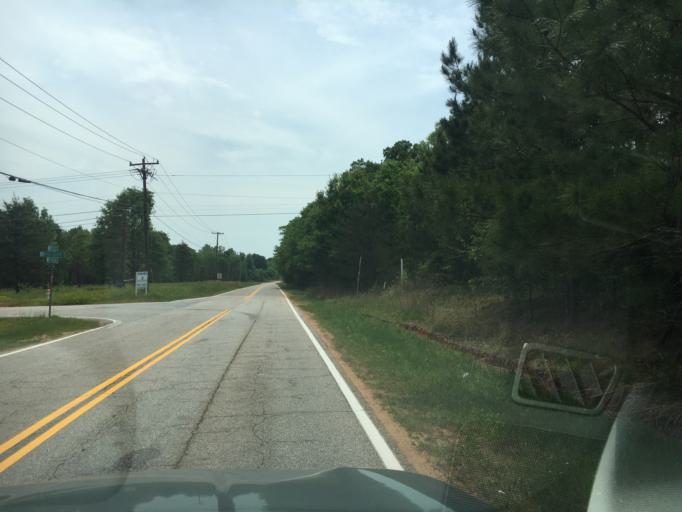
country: US
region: South Carolina
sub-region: Spartanburg County
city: Fairforest
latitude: 34.9714
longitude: -82.0103
